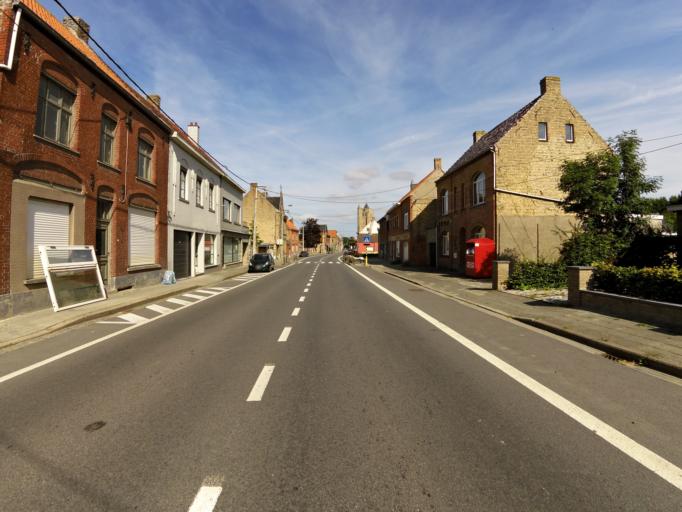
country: BE
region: Flanders
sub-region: Provincie West-Vlaanderen
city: Diksmuide
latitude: 51.0273
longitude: 2.9051
